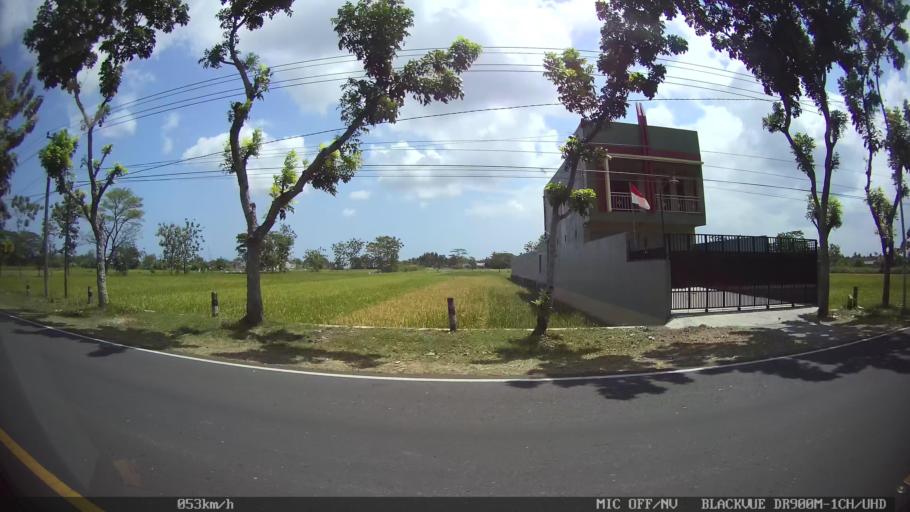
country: ID
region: Daerah Istimewa Yogyakarta
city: Sewon
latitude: -7.8904
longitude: 110.3474
